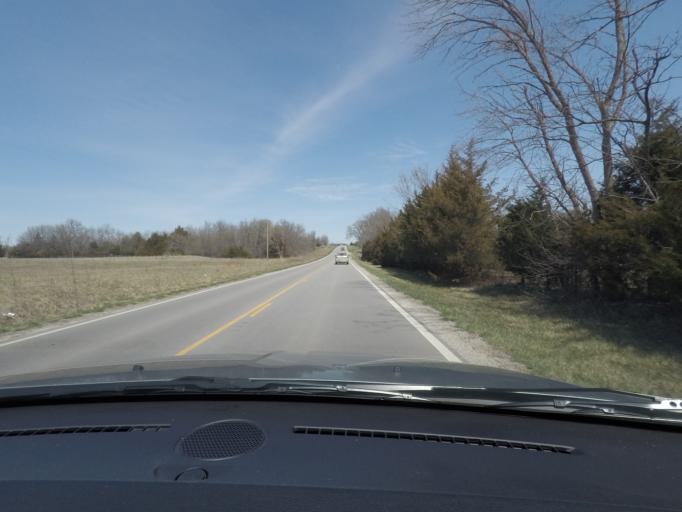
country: US
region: Kansas
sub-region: Lyon County
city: Emporia
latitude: 38.4872
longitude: -96.1709
